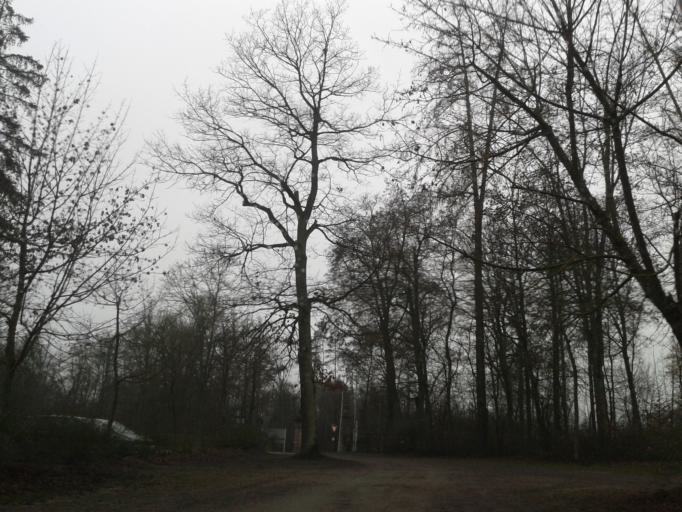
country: DE
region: Bavaria
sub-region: Upper Franconia
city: Weitramsdorf
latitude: 50.2325
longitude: 10.8637
